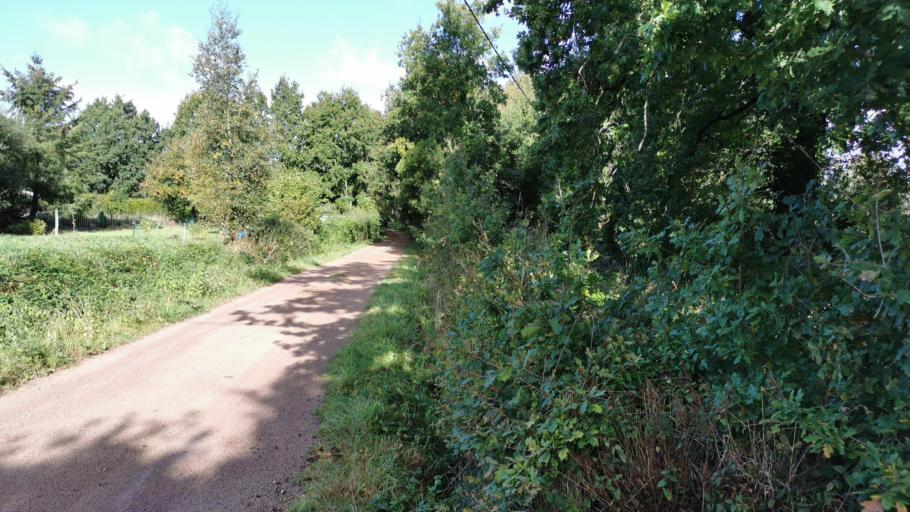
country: FR
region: Brittany
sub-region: Departement d'Ille-et-Vilaine
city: Plelan-le-Grand
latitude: 47.9988
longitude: -2.1085
